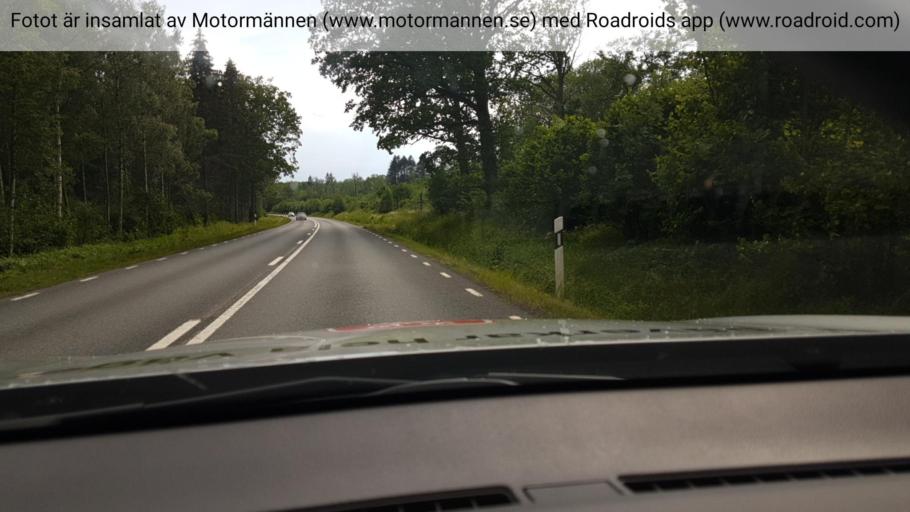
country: SE
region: Vaestra Goetaland
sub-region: Hjo Kommun
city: Hjo
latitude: 58.1164
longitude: 14.2113
